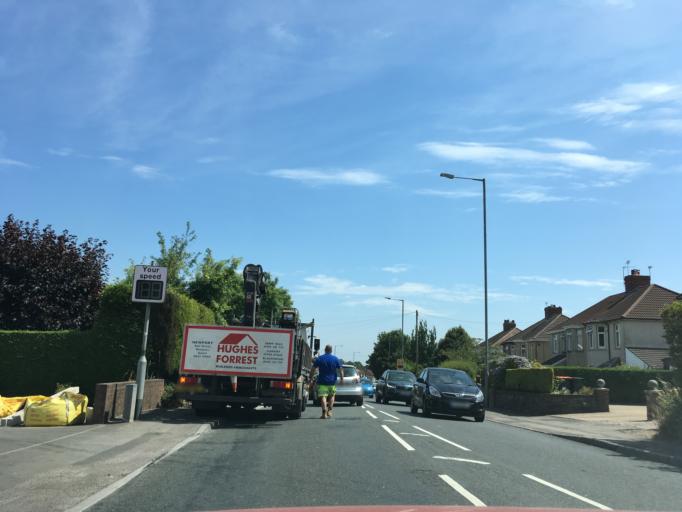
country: GB
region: Wales
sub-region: Newport
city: Newport
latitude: 51.5879
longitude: -3.0395
